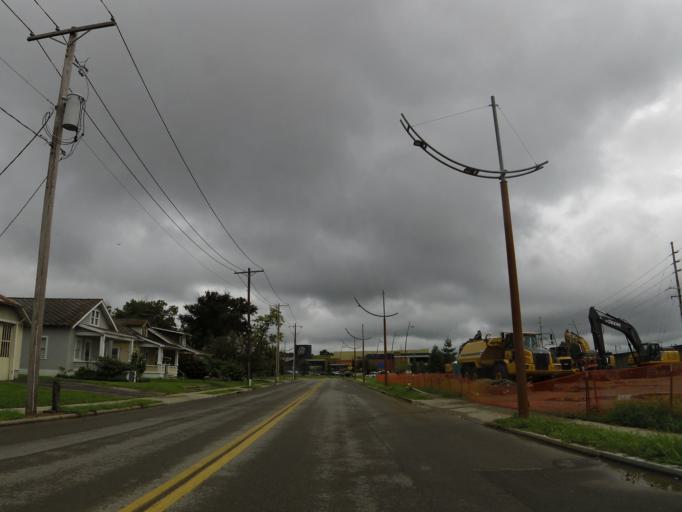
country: US
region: Missouri
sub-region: Cape Girardeau County
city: Cape Girardeau
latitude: 37.3100
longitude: -89.5177
